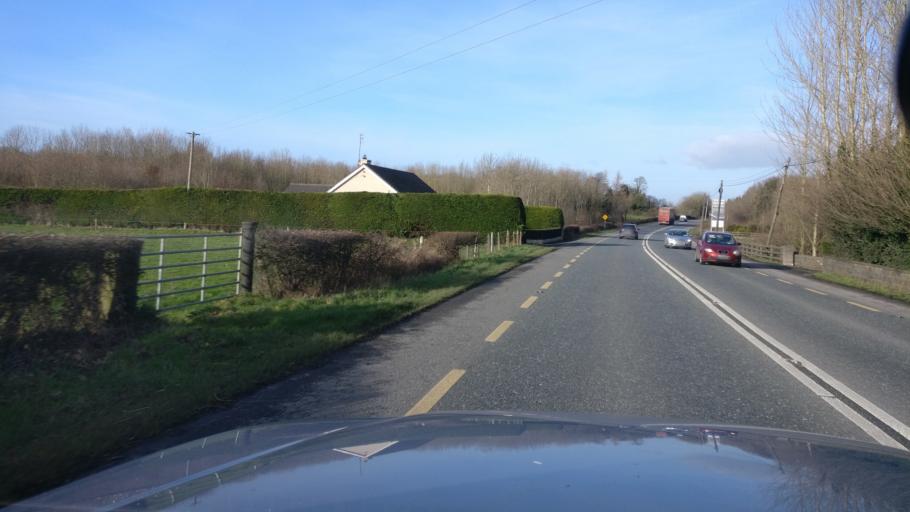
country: IE
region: Leinster
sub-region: Uibh Fhaili
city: Tullamore
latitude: 53.2258
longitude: -7.4760
